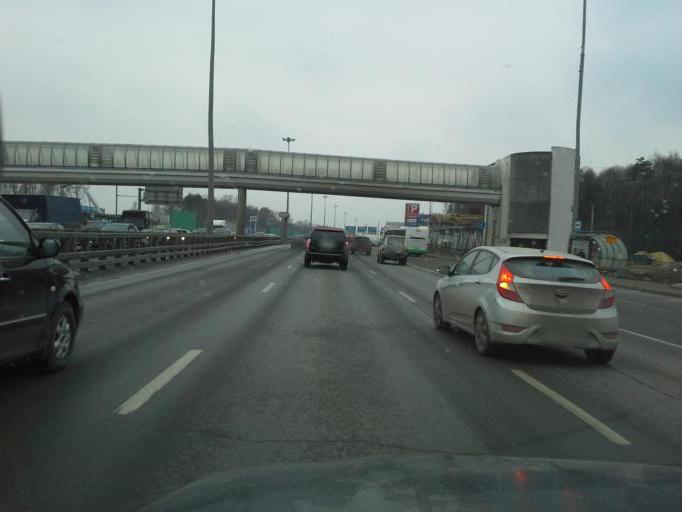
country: RU
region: Moskovskaya
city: Mosrentgen
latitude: 55.6362
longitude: 37.4538
